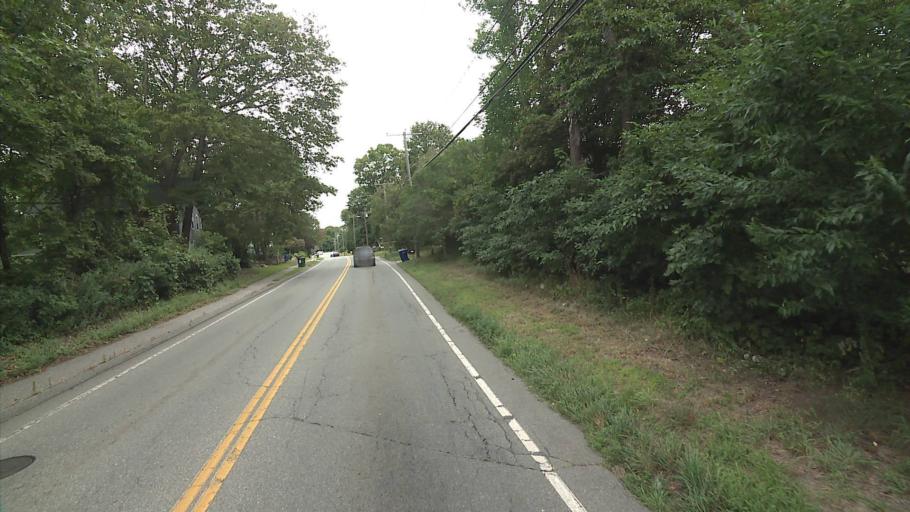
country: US
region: Connecticut
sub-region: New London County
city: Central Waterford
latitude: 41.3316
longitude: -72.1557
